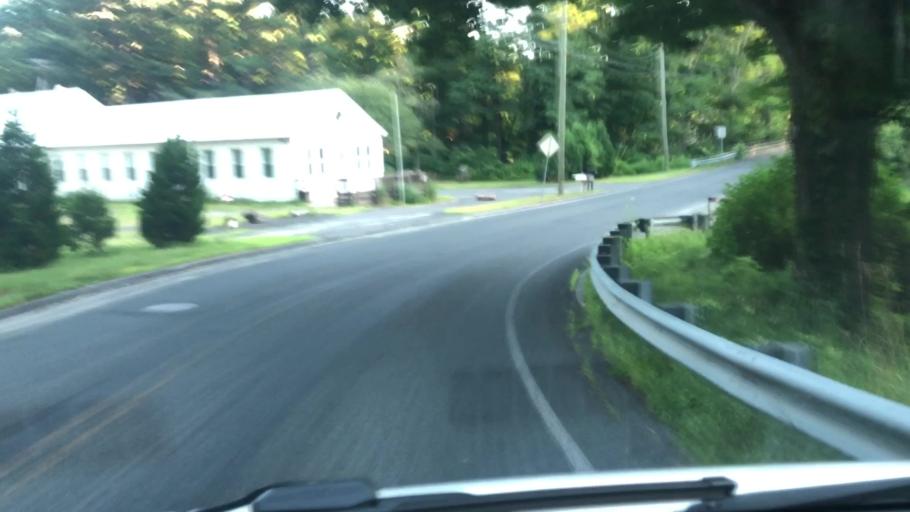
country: US
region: Massachusetts
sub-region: Hampshire County
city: Easthampton
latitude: 42.2757
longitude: -72.7165
